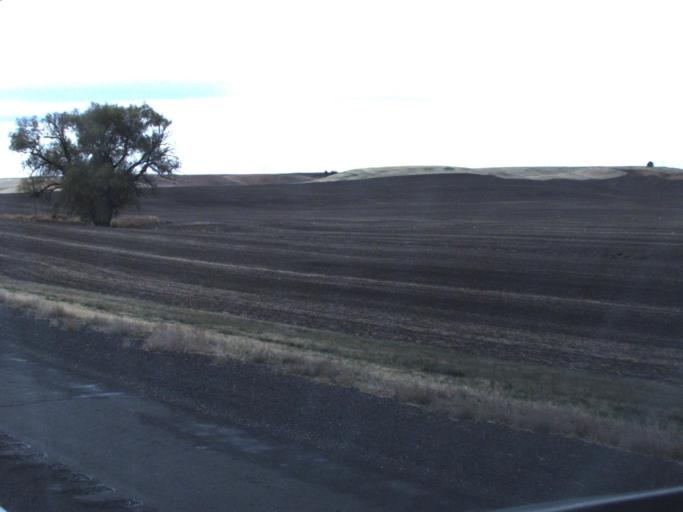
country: US
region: Washington
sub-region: Asotin County
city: Clarkston
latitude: 46.5089
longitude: -117.0794
